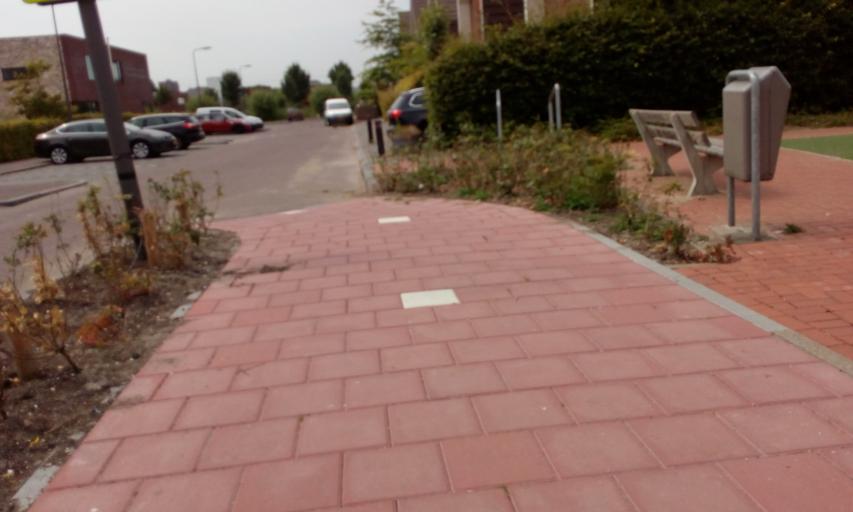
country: NL
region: South Holland
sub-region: Gemeente Krimpen aan den IJssel
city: Krimpen aan den IJssel
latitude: 51.9540
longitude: 4.6113
